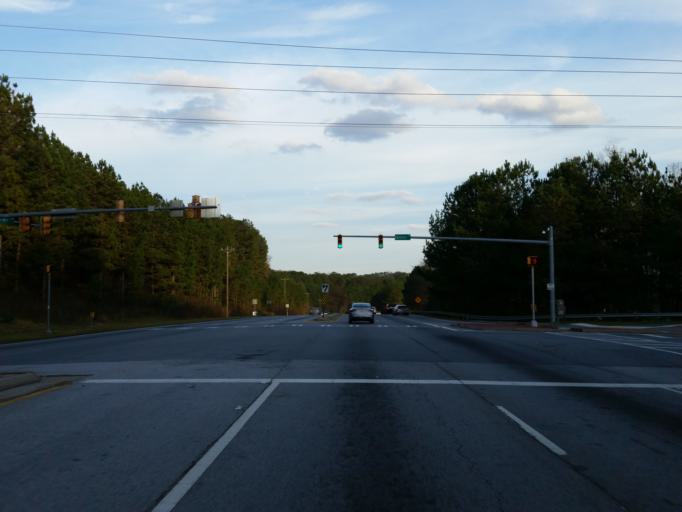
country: US
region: Georgia
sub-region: Cobb County
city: Smyrna
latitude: 33.8455
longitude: -84.5391
